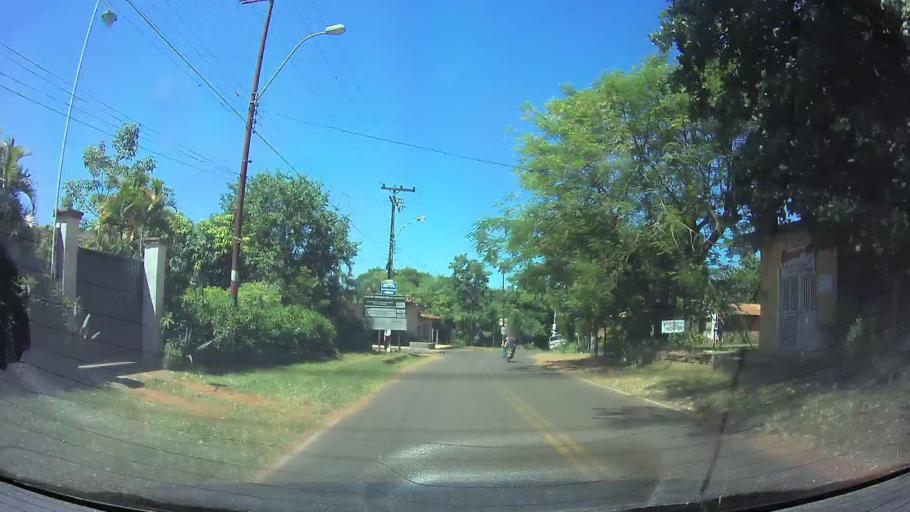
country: PY
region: Central
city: Aregua
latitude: -25.2899
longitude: -57.4095
